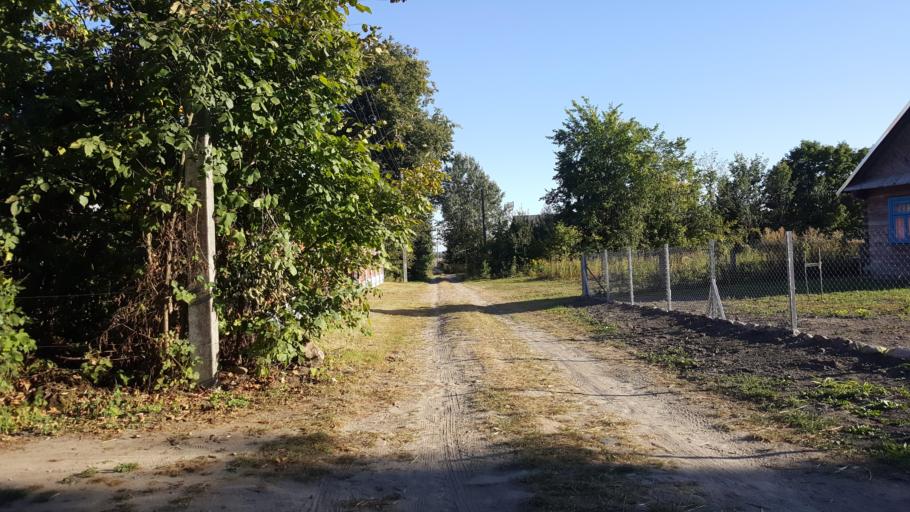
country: BY
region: Brest
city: Vysokaye
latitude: 52.3334
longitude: 23.2970
